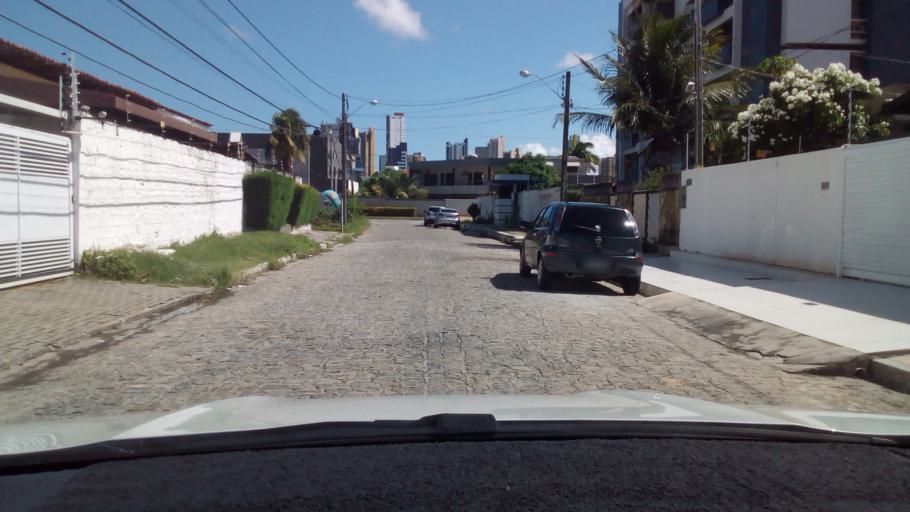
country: BR
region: Paraiba
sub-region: Joao Pessoa
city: Joao Pessoa
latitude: -7.0919
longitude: -34.8386
